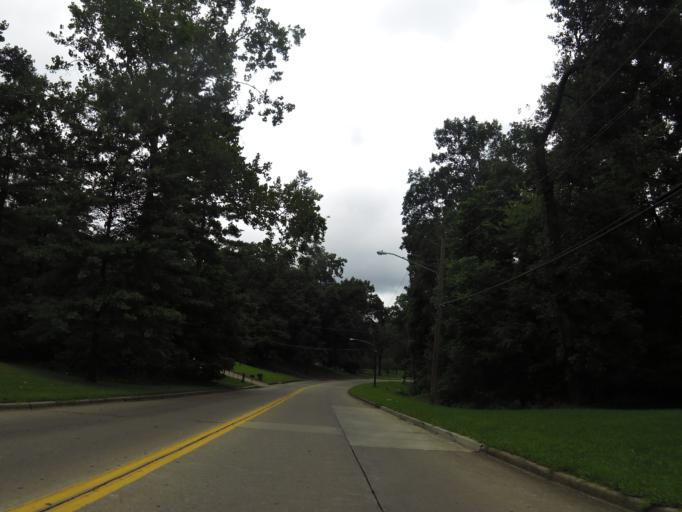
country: US
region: Missouri
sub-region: Cape Girardeau County
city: Cape Girardeau
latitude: 37.3255
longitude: -89.5511
